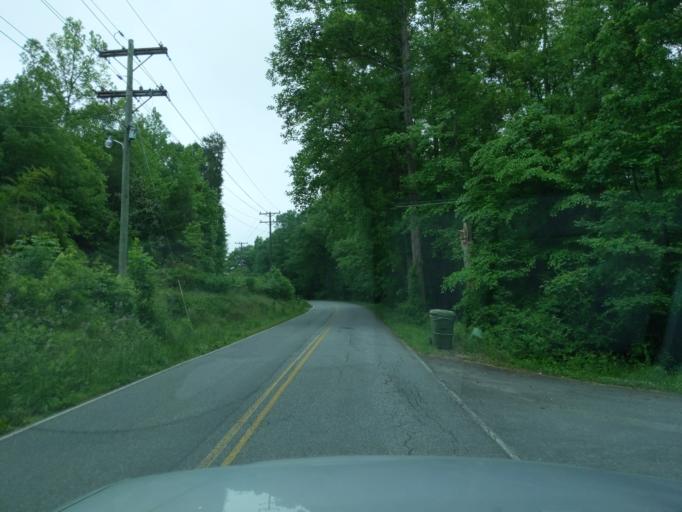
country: US
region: South Carolina
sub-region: Greenville County
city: Five Forks
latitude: 34.8386
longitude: -82.1824
